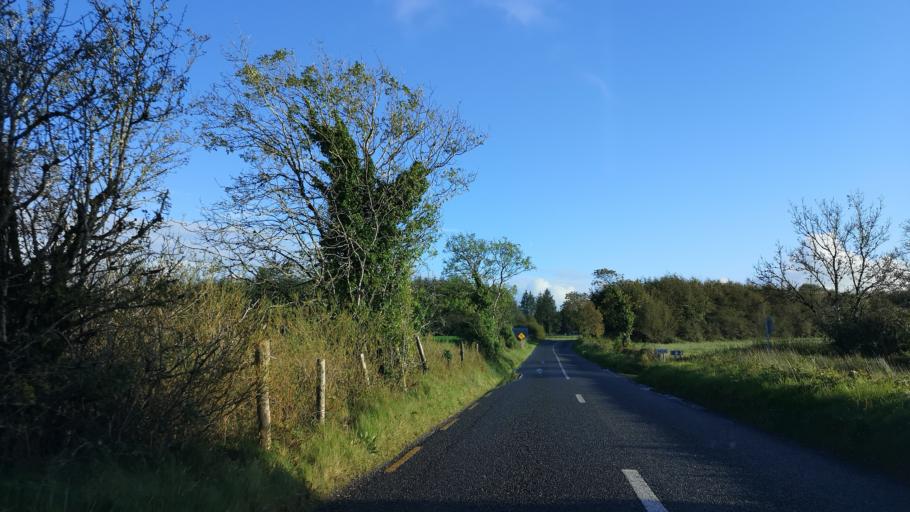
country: IE
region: Connaught
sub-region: Roscommon
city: Castlerea
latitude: 53.8035
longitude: -8.5038
